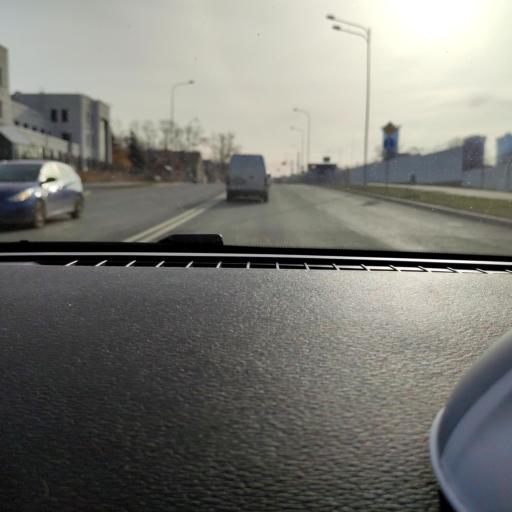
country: RU
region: Samara
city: Samara
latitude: 53.2106
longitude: 50.1506
